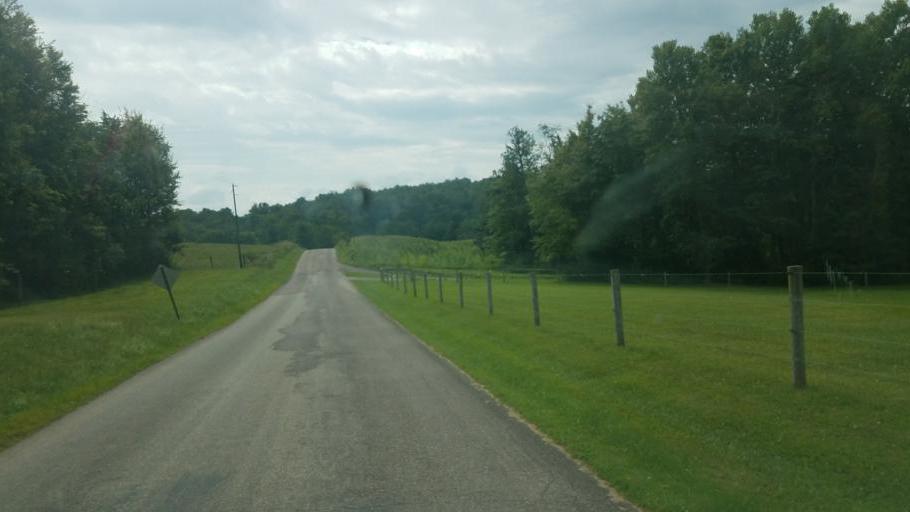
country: US
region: Ohio
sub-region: Ashland County
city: Loudonville
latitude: 40.5584
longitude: -82.3610
